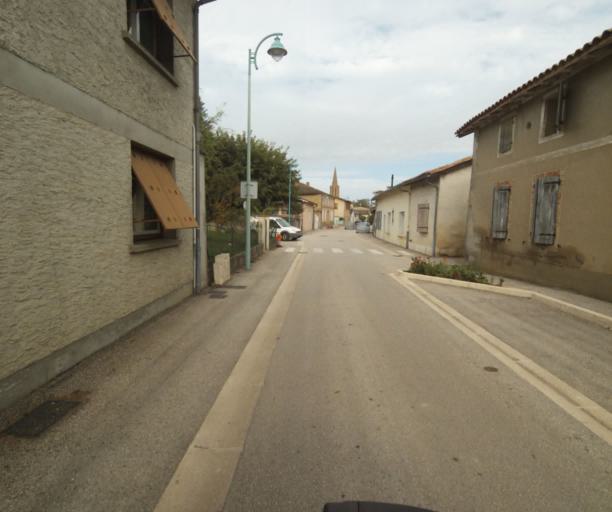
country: FR
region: Midi-Pyrenees
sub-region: Departement du Tarn-et-Garonne
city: Finhan
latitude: 43.9107
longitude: 1.2219
